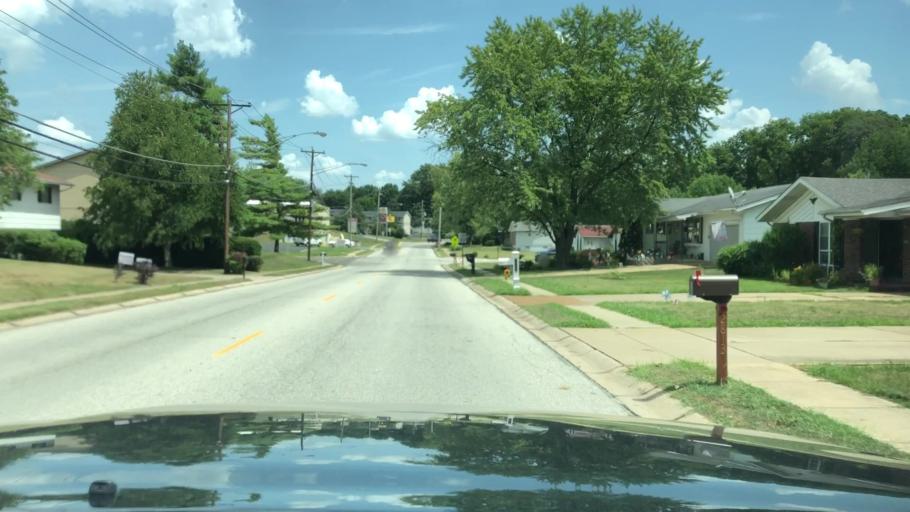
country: US
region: Missouri
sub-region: Saint Charles County
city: Saint Charles
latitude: 38.7928
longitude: -90.5189
